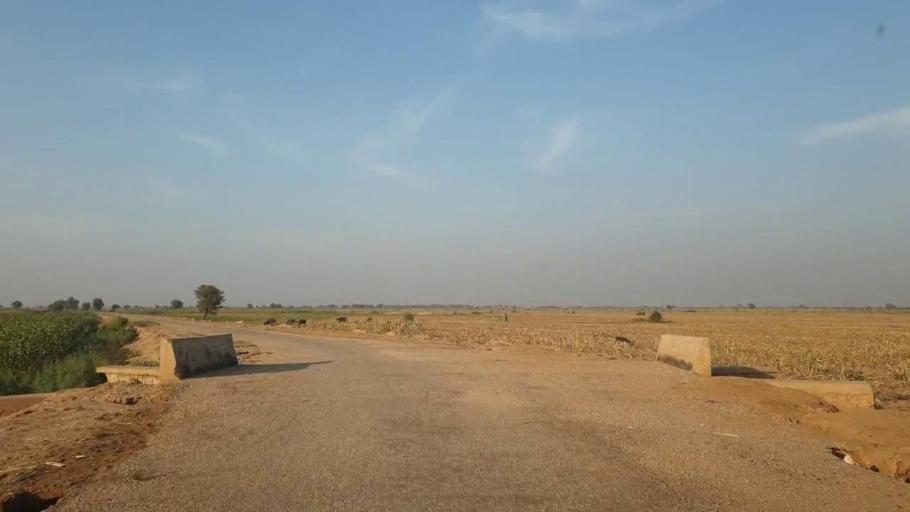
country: PK
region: Sindh
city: Sann
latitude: 25.9224
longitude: 68.1796
